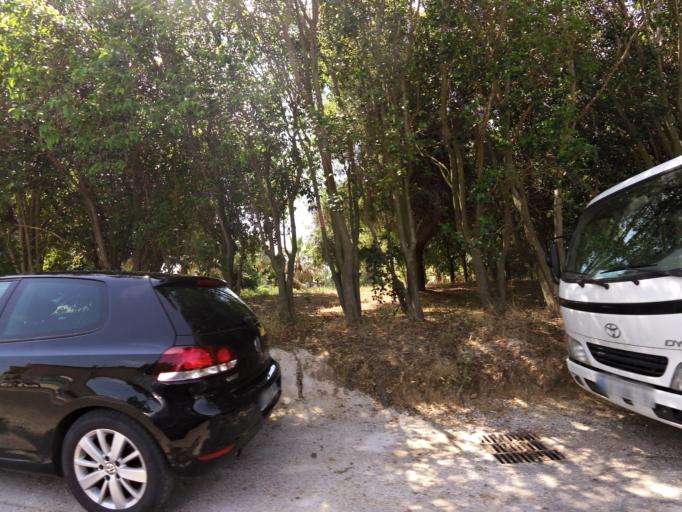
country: FR
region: Provence-Alpes-Cote d'Azur
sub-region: Departement du Var
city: Hyeres
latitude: 43.1160
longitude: 6.1379
